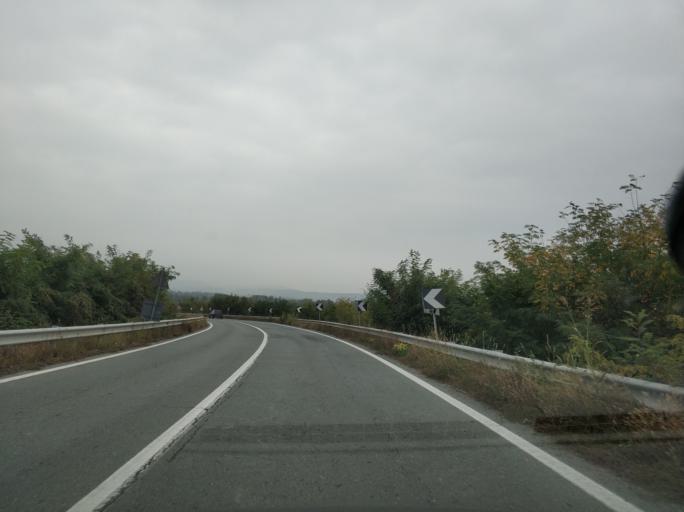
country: IT
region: Piedmont
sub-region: Provincia di Torino
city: Rivarolo Canavese
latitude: 45.3220
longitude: 7.7333
